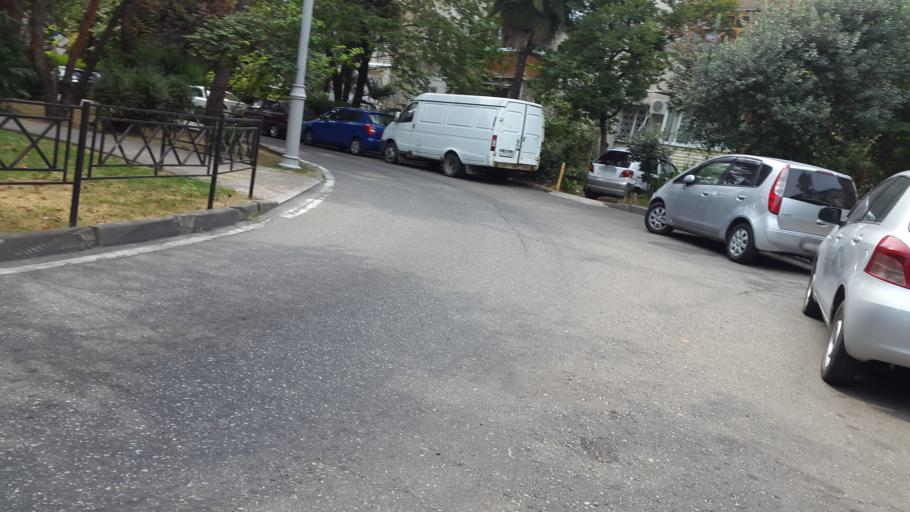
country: RU
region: Krasnodarskiy
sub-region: Sochi City
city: Sochi
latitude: 43.6026
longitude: 39.7249
